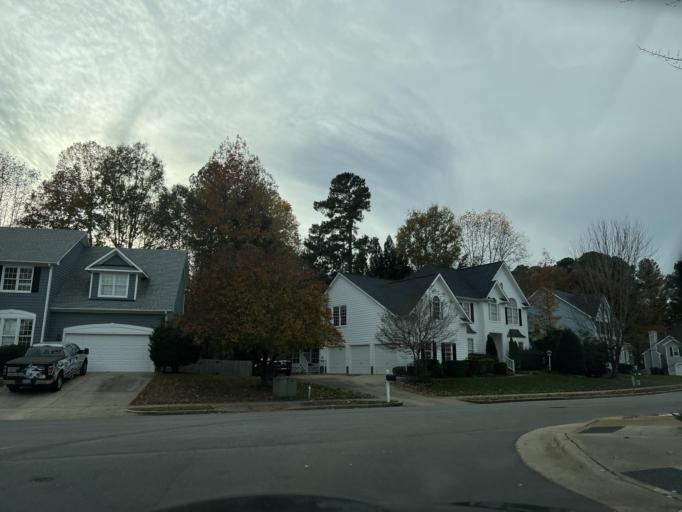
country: US
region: North Carolina
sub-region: Wake County
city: Wake Forest
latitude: 35.8928
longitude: -78.5935
